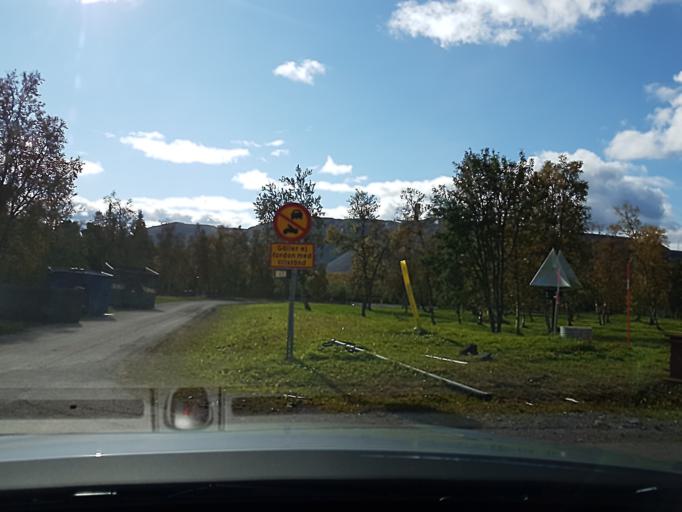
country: SE
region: Norrbotten
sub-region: Kiruna Kommun
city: Kiruna
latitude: 67.8485
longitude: 20.2236
